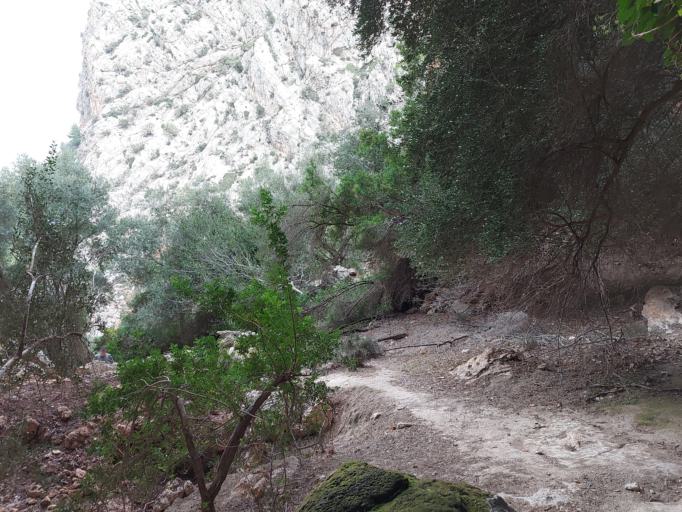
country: ES
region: Balearic Islands
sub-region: Illes Balears
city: Fornalutx
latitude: 39.7680
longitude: 2.7459
